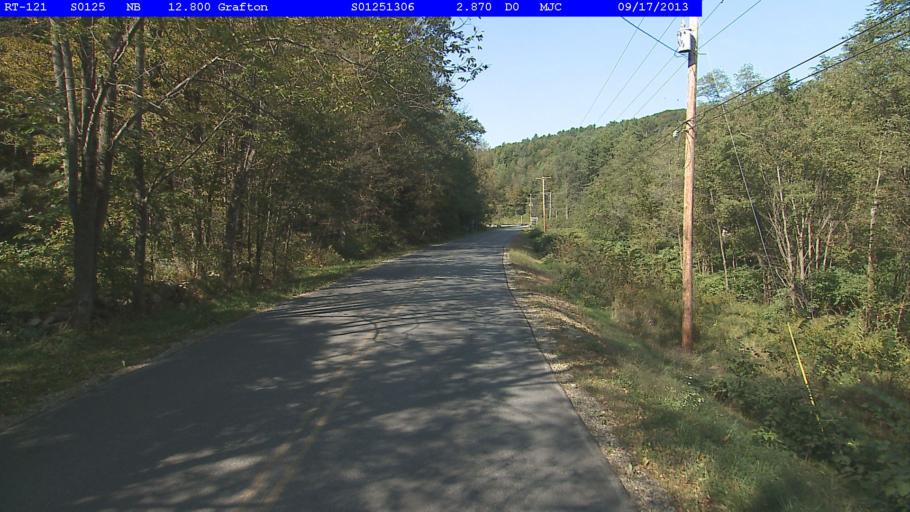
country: US
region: Vermont
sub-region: Windsor County
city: Chester
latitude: 43.1771
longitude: -72.5864
